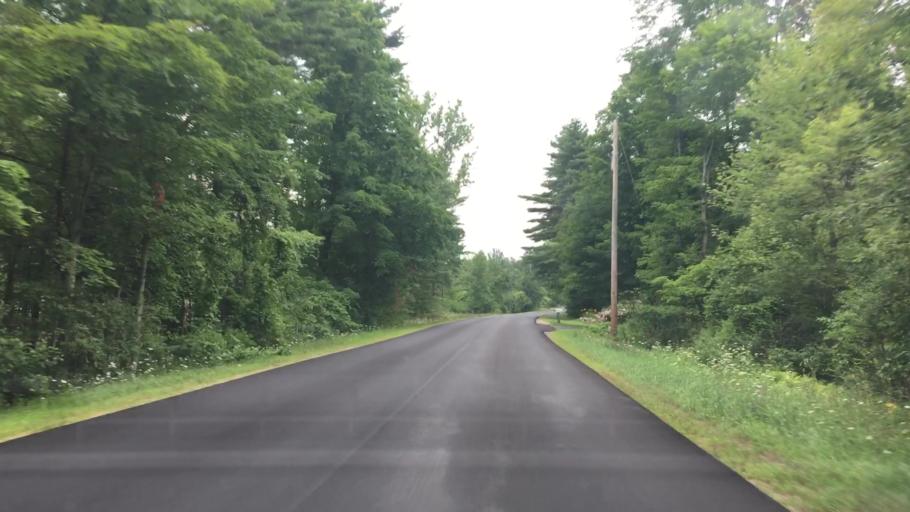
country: US
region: New York
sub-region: Clinton County
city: Peru
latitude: 44.5798
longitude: -73.5700
